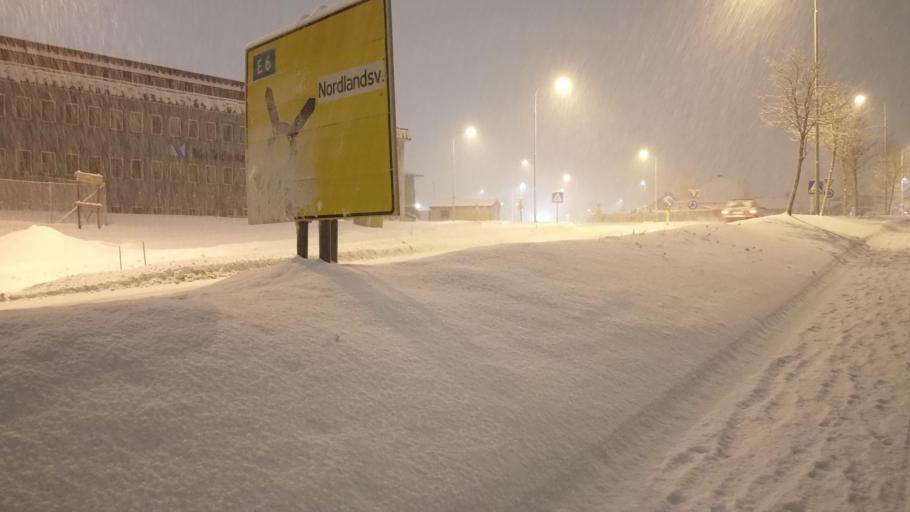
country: NO
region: Nordland
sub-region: Rana
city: Mo i Rana
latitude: 66.3145
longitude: 14.1614
